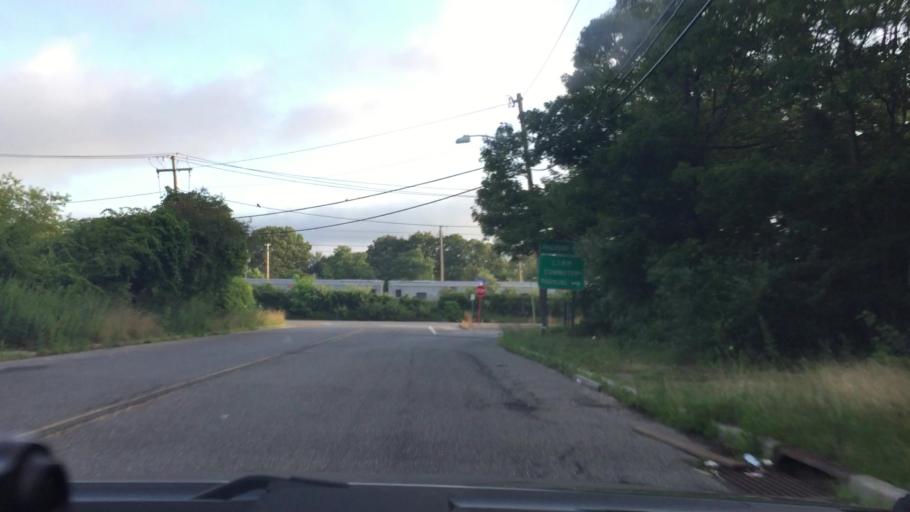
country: US
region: New York
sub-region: Suffolk County
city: Ronkonkoma
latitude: 40.8068
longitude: -73.1121
